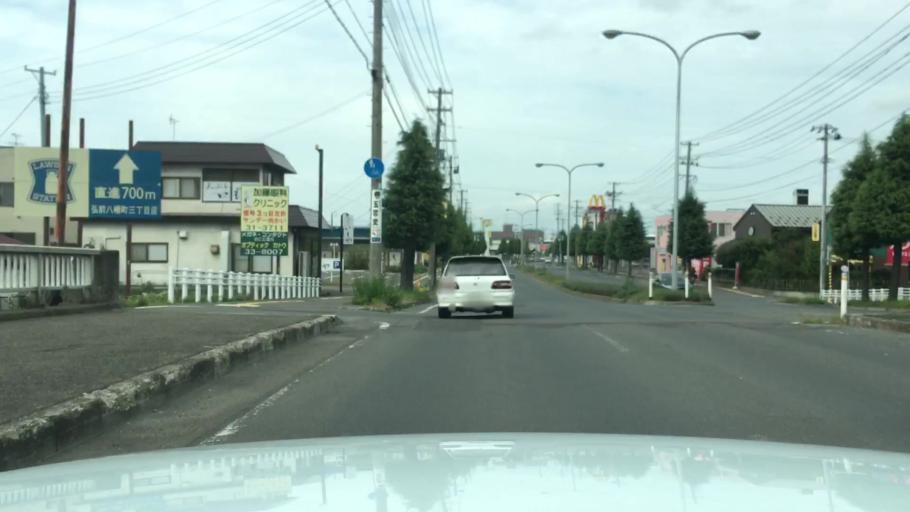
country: JP
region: Aomori
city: Hirosaki
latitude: 40.6105
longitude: 140.4816
